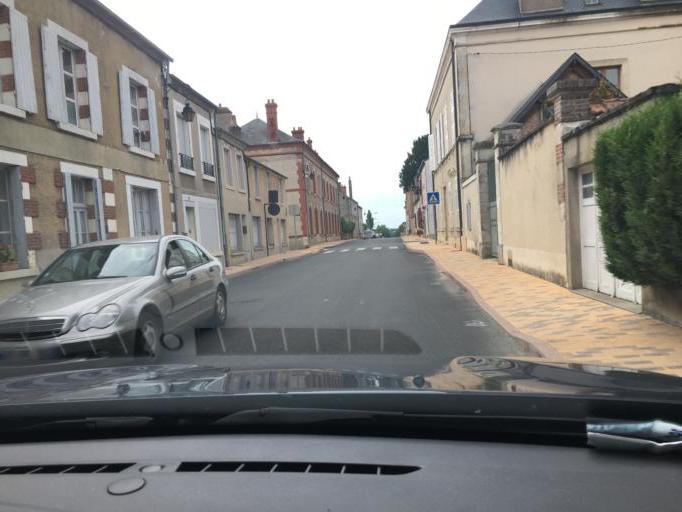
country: FR
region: Centre
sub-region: Departement du Cher
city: Henrichemont
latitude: 47.3035
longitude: 2.5237
